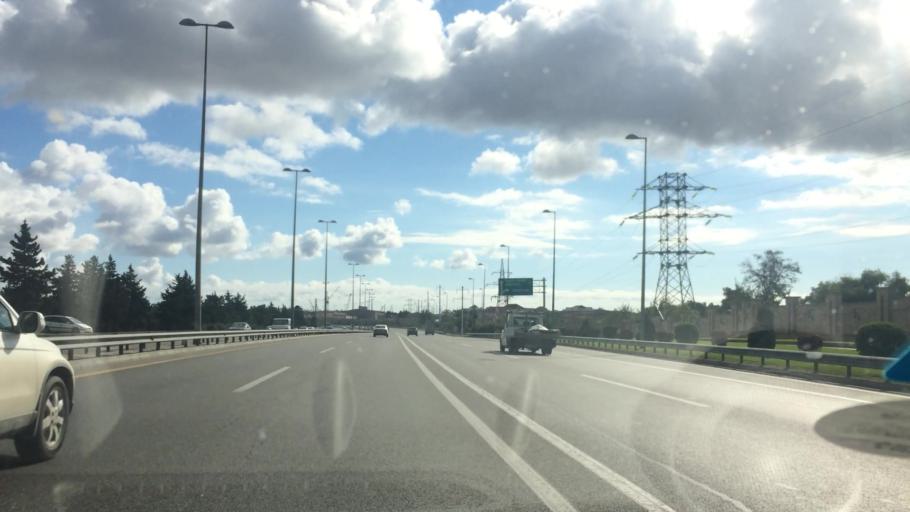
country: AZ
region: Baki
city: Ramana
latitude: 40.4399
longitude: 49.9709
